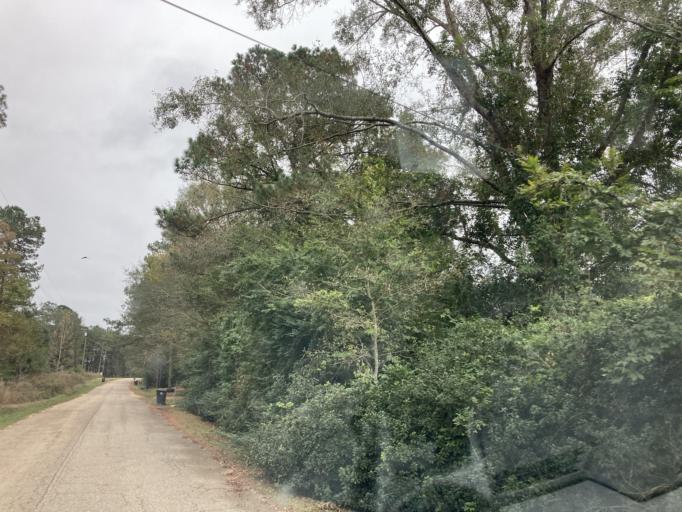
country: US
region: Mississippi
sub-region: Lamar County
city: West Hattiesburg
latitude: 31.2580
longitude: -89.5090
